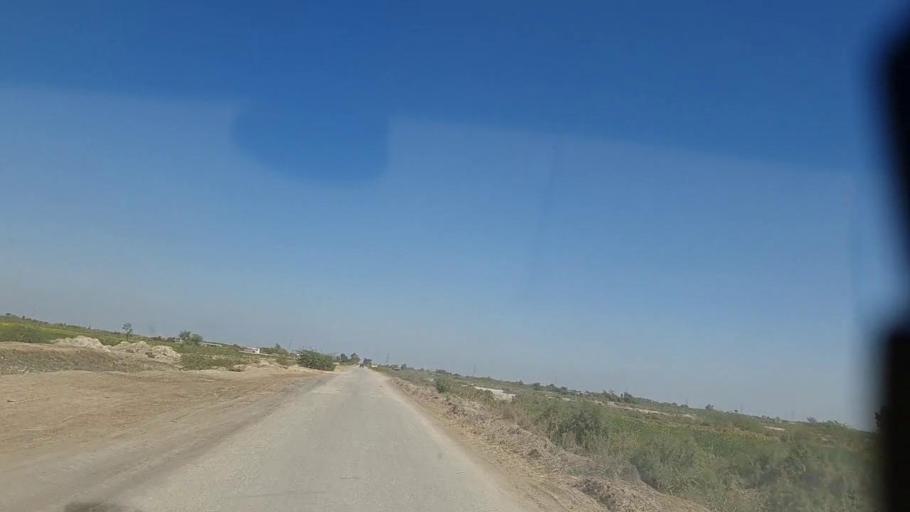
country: PK
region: Sindh
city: Mirwah Gorchani
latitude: 25.2465
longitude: 69.0351
